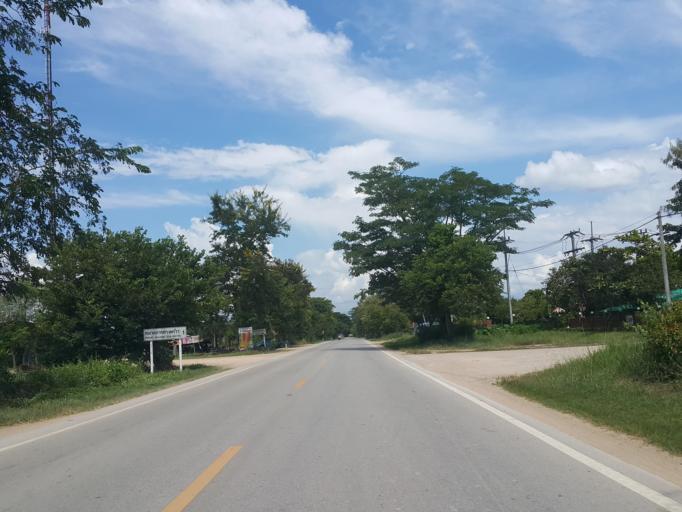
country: TH
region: Chiang Mai
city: Phrao
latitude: 19.3097
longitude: 99.1899
